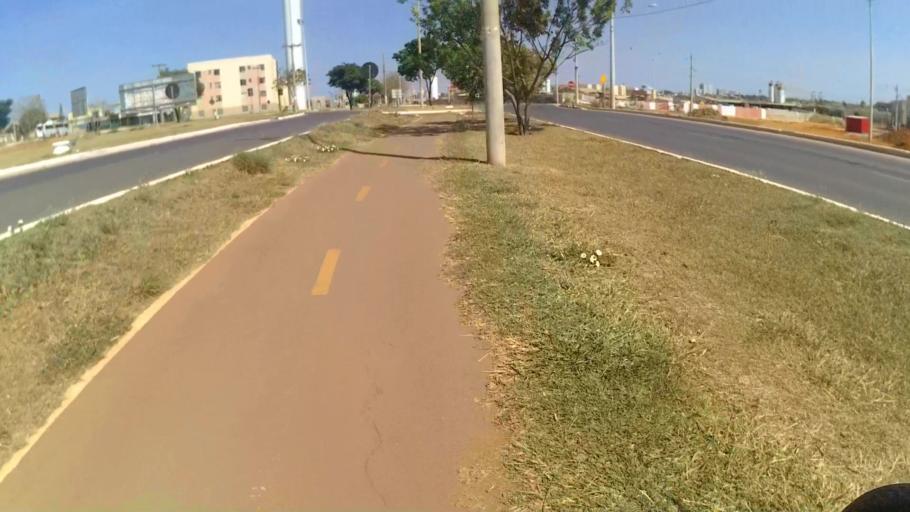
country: BR
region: Federal District
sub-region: Brasilia
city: Brasilia
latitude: -15.8938
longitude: -48.0456
